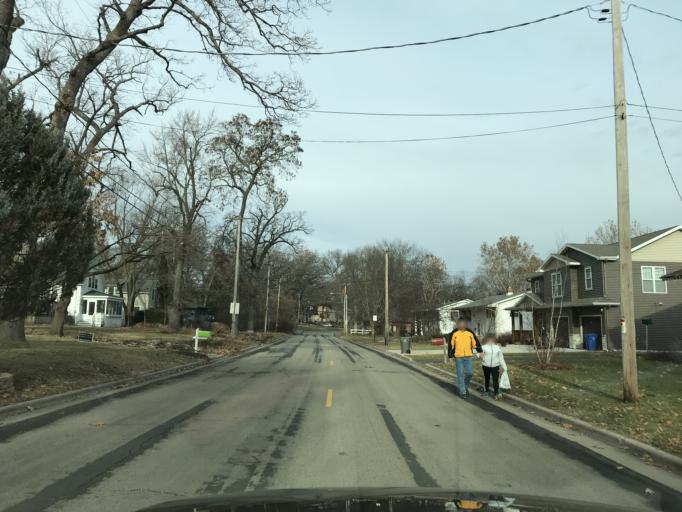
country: US
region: Wisconsin
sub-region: Dane County
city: Monona
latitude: 43.0638
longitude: -89.3451
